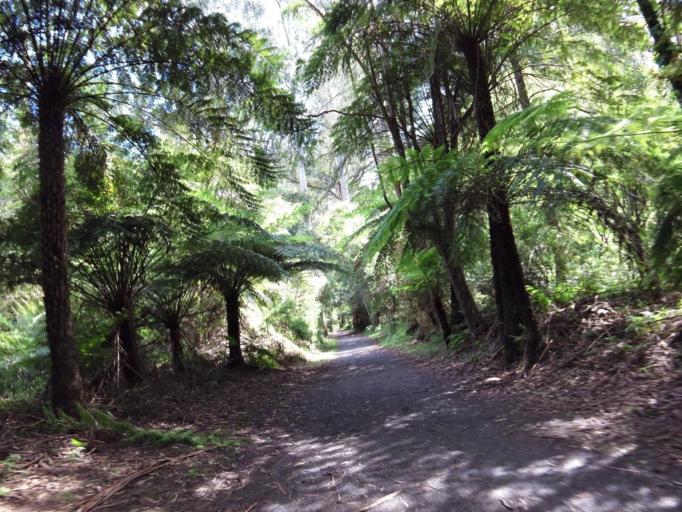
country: AU
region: Victoria
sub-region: Yarra Ranges
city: Millgrove
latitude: -37.7490
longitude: 145.7124
